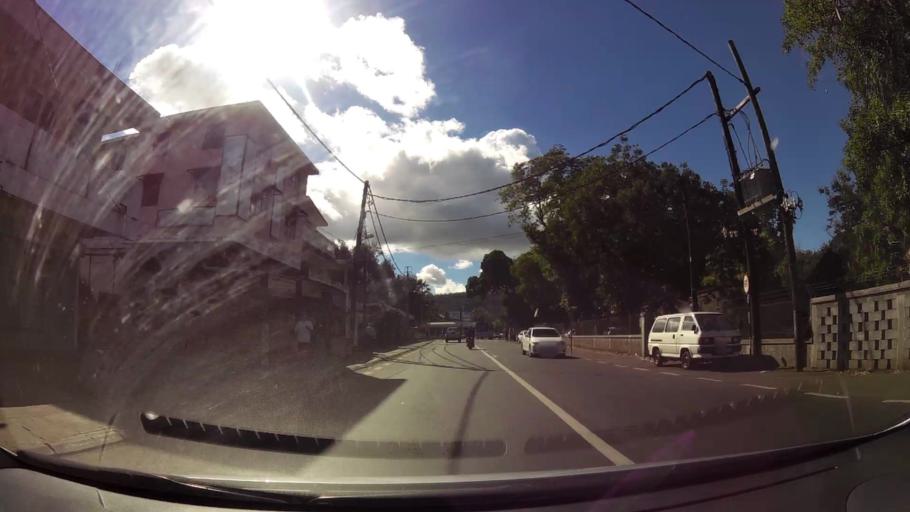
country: MU
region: Pamplemousses
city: Le Hochet
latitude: -20.1470
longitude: 57.5224
